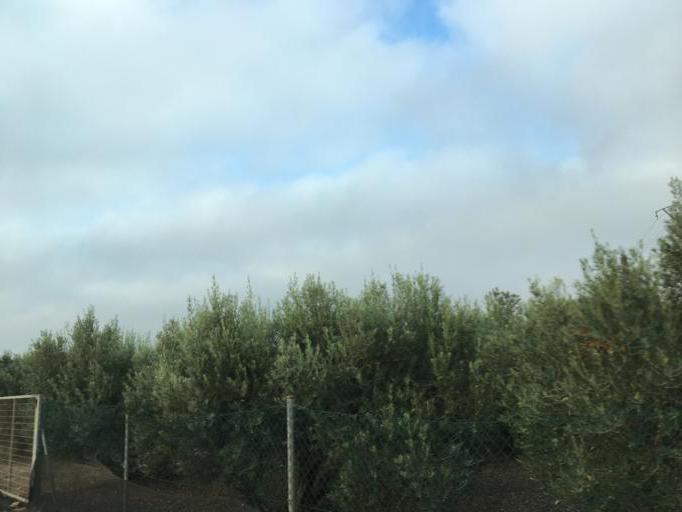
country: ES
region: Murcia
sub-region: Murcia
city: La Union
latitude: 37.6659
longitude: -0.9371
